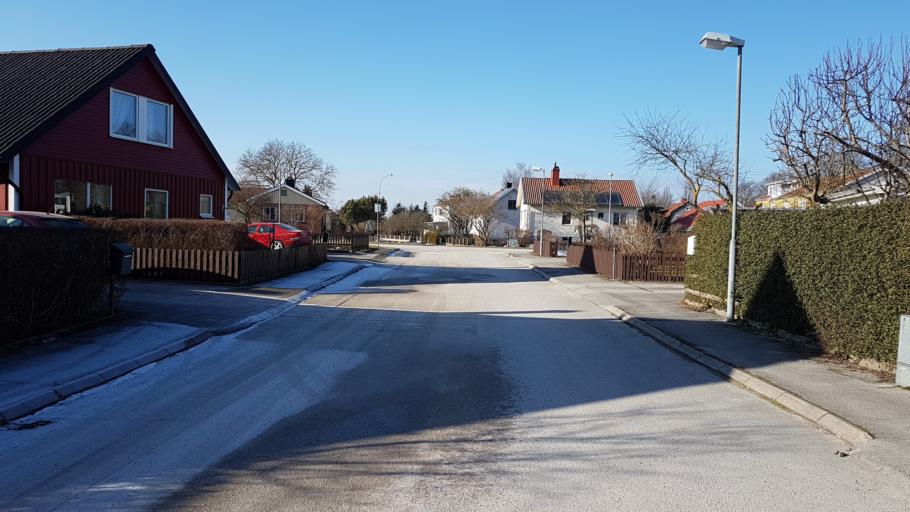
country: SE
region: Gotland
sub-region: Gotland
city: Visby
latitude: 57.6330
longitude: 18.3205
